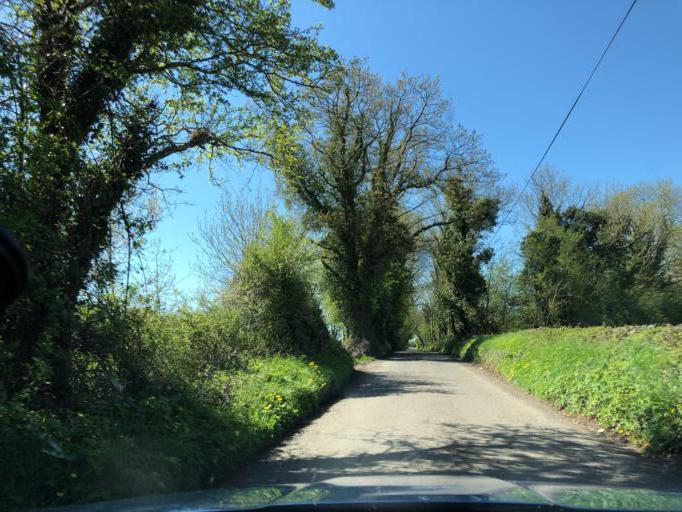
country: IE
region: Connaught
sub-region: County Galway
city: Portumna
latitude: 53.1532
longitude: -8.3355
